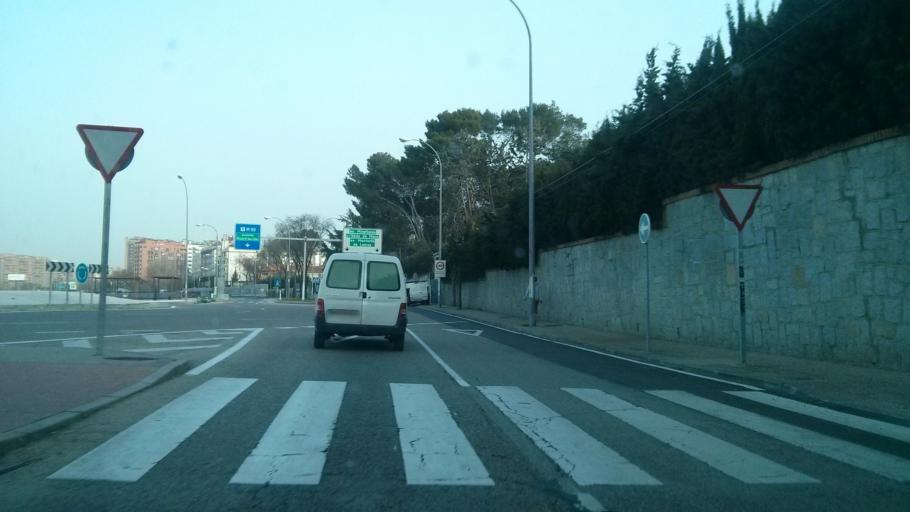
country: ES
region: Madrid
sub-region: Provincia de Madrid
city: Tetuan de las Victorias
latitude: 40.4730
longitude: -3.7359
